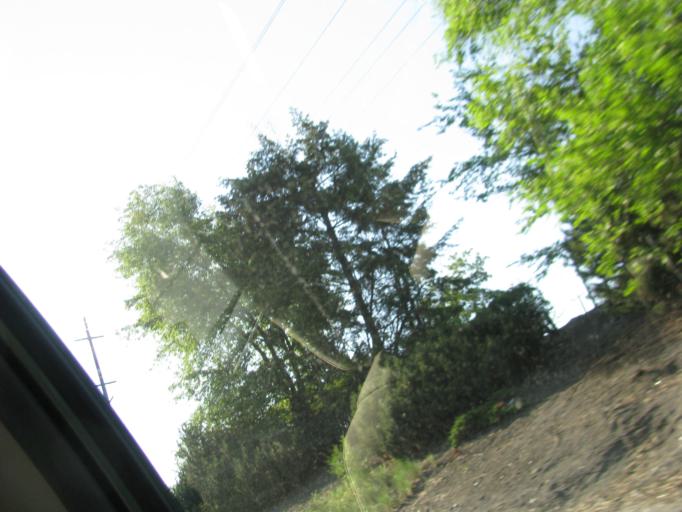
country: US
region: Washington
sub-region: Spokane County
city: Spokane
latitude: 47.6541
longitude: -117.3629
